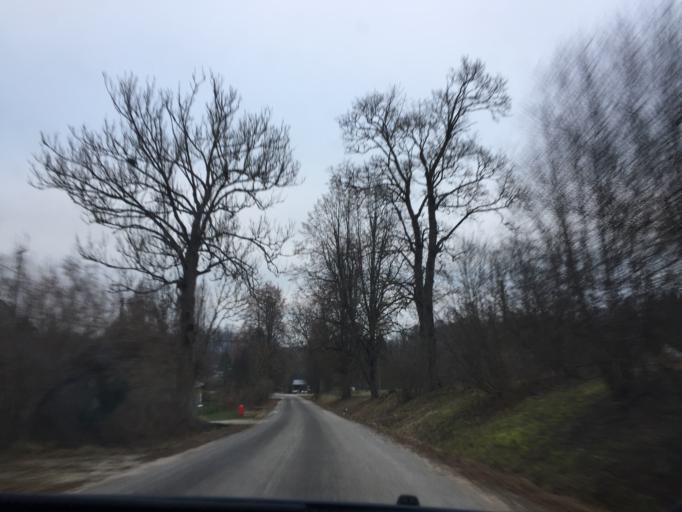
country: LV
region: Raunas
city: Rauna
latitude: 57.3247
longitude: 25.6001
